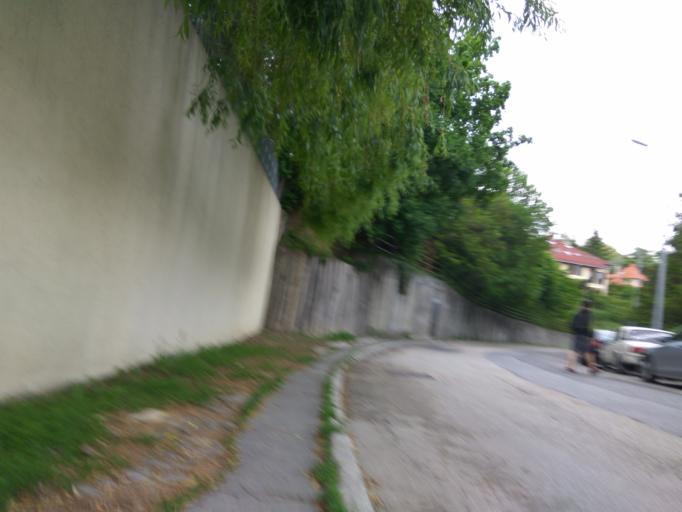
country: HU
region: Budapest
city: Budapest XII. keruelet
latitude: 47.4973
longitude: 18.9982
